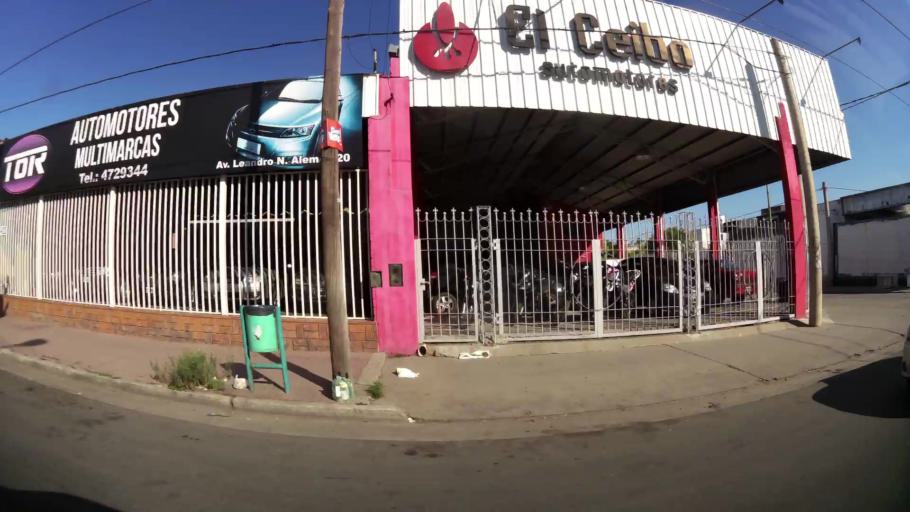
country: AR
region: Cordoba
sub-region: Departamento de Capital
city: Cordoba
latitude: -31.3878
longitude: -64.1612
